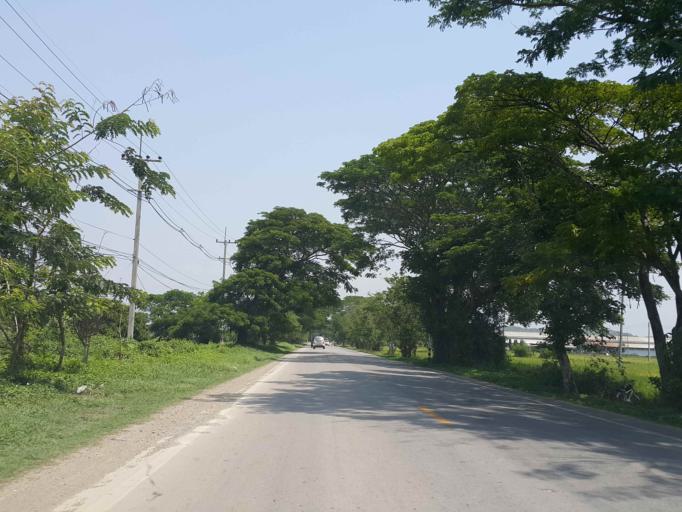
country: TH
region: Chiang Mai
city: Mae Taeng
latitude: 19.0583
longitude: 98.9592
